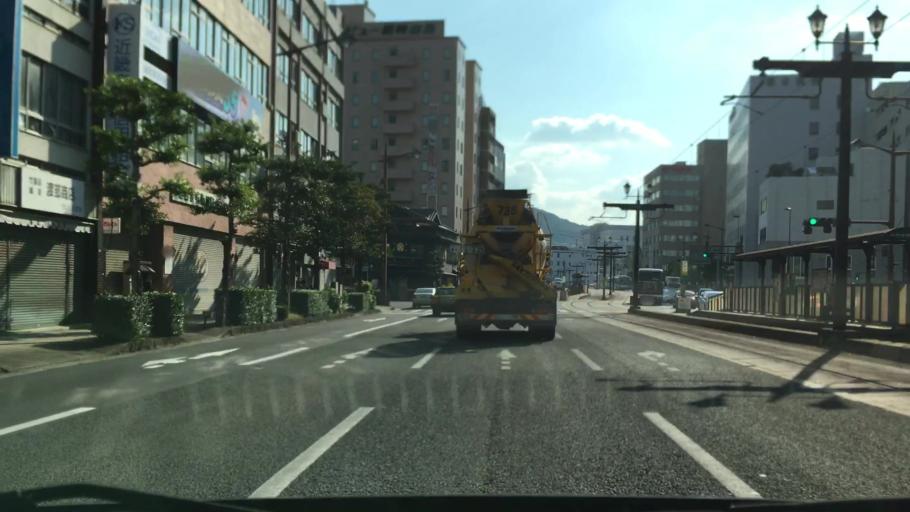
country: JP
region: Nagasaki
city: Nagasaki-shi
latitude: 32.7465
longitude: 129.8723
